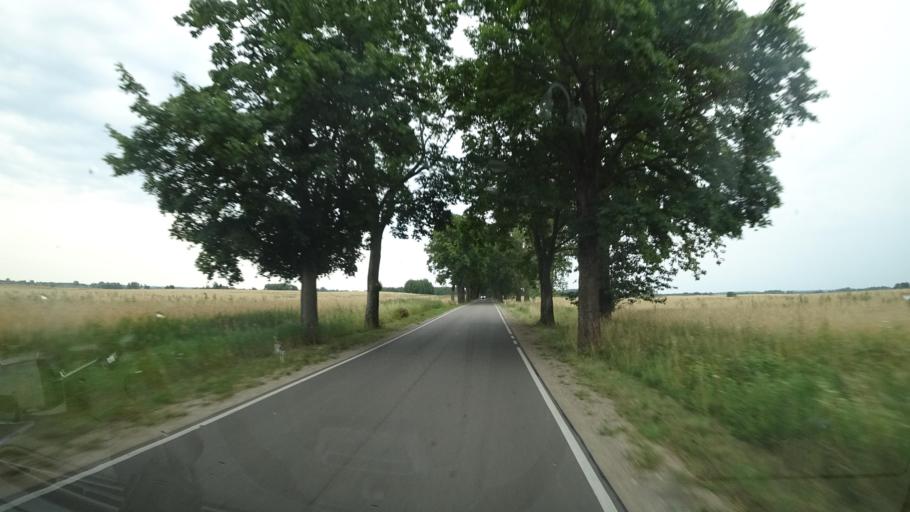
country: PL
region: Warmian-Masurian Voivodeship
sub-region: Powiat mragowski
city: Mikolajki
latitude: 53.8601
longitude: 21.6060
